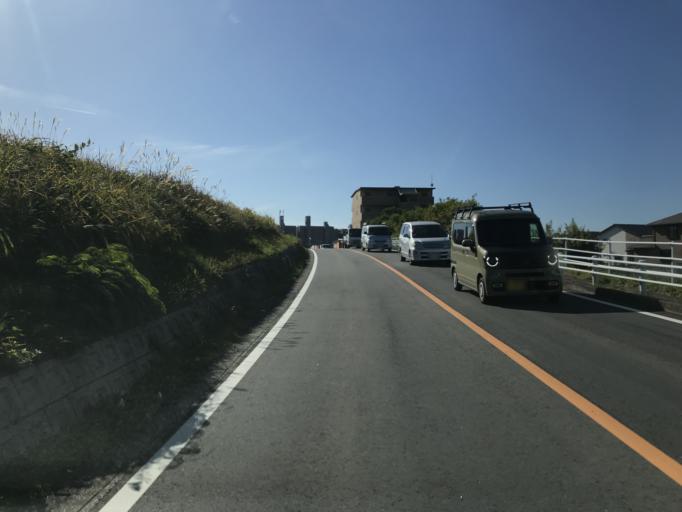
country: JP
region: Aichi
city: Kanie
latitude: 35.1688
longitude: 136.8270
